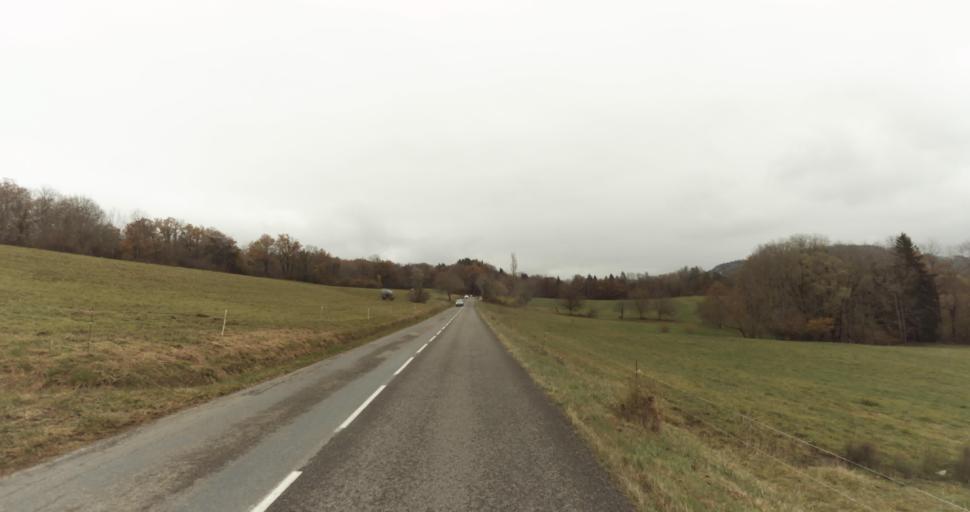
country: FR
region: Rhone-Alpes
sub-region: Departement de la Haute-Savoie
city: Evires
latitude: 46.0242
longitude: 6.2019
